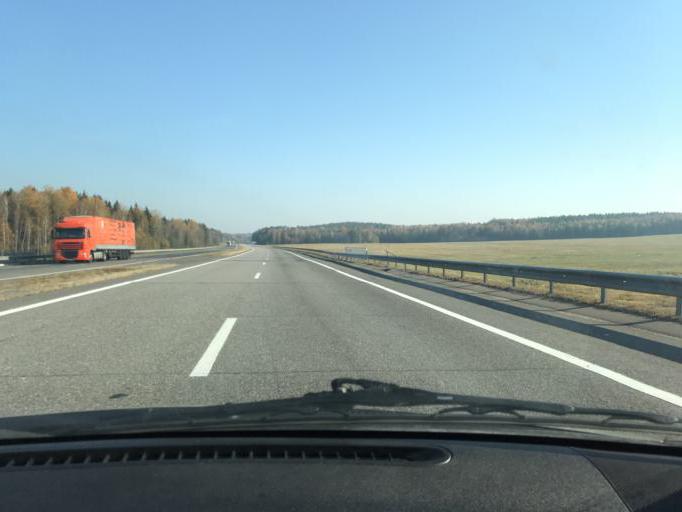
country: BY
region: Vitebsk
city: Talachyn
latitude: 54.4118
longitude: 29.5039
